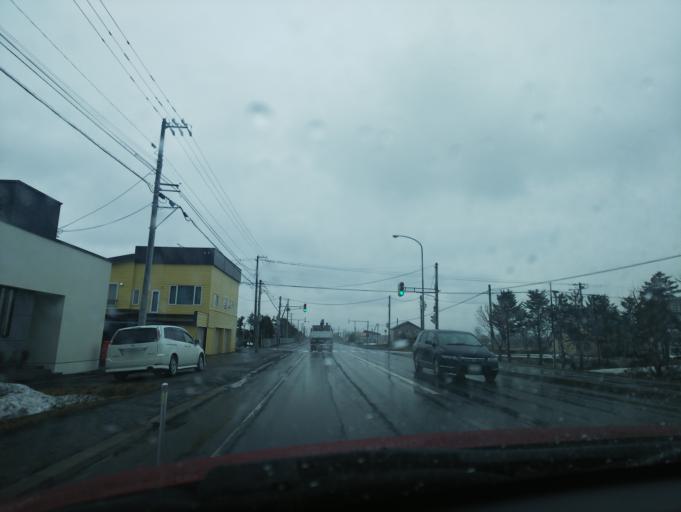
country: JP
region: Hokkaido
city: Nayoro
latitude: 44.2103
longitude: 142.3948
